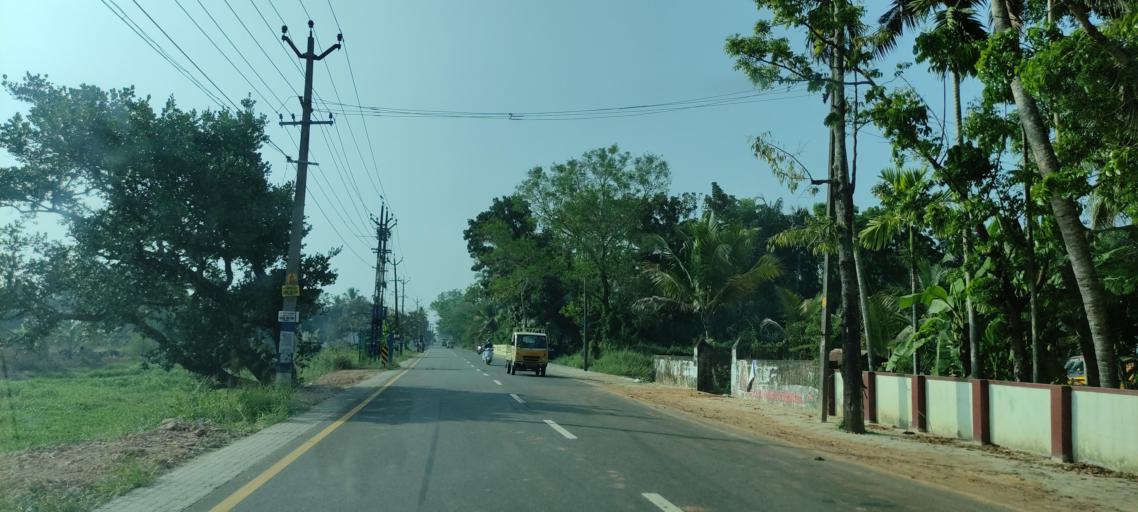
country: IN
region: Kerala
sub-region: Kottayam
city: Changanacheri
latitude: 9.3636
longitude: 76.4452
